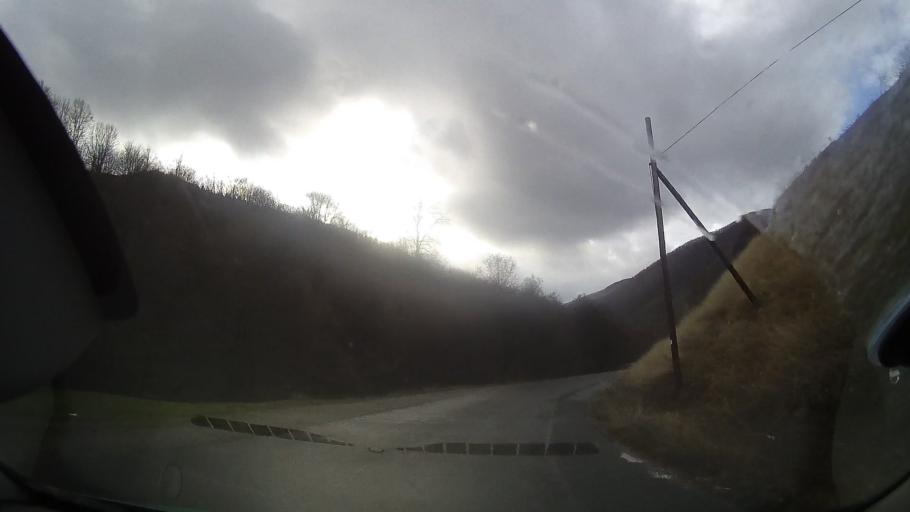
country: RO
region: Alba
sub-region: Comuna Rimetea
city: Rimetea
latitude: 46.4988
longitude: 23.5879
